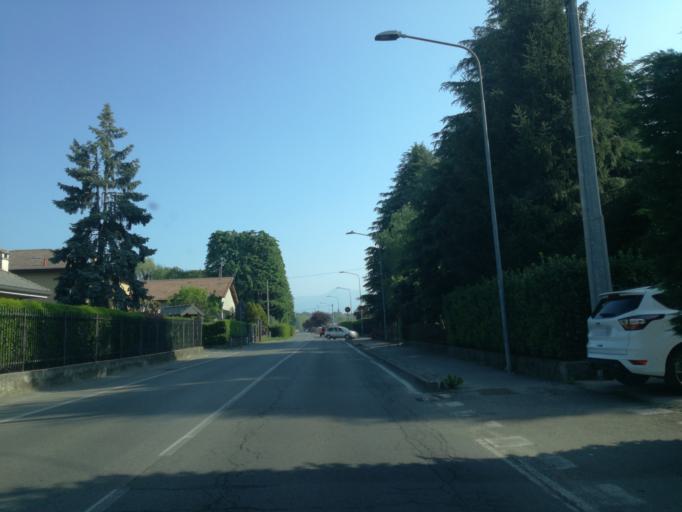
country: IT
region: Lombardy
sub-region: Provincia di Lecco
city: Merate
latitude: 45.6829
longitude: 9.4117
